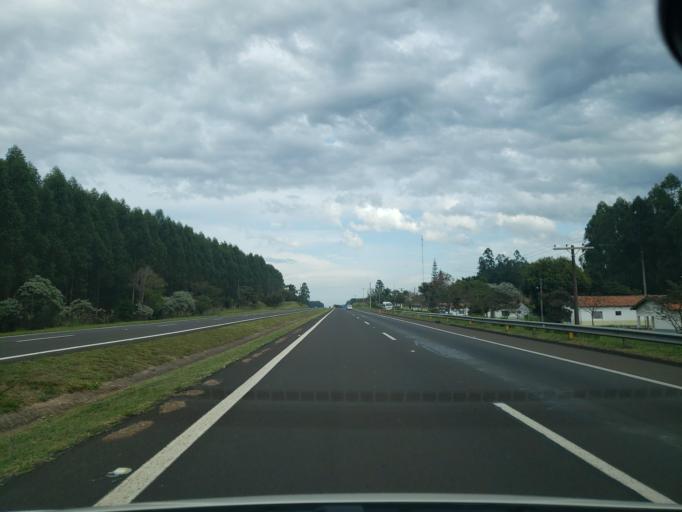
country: BR
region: Sao Paulo
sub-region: Itirapina
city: Itirapina
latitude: -22.2595
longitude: -47.8751
